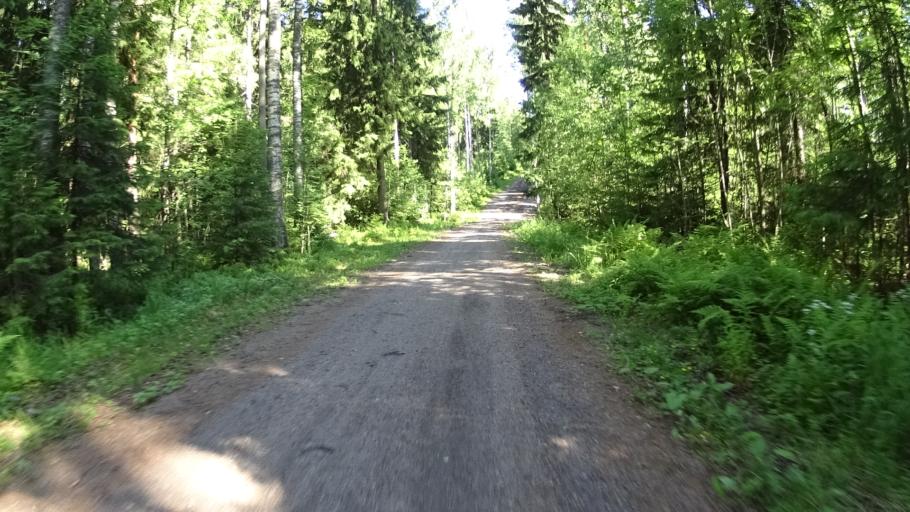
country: FI
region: Uusimaa
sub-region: Helsinki
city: Kilo
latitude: 60.3101
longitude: 24.8089
